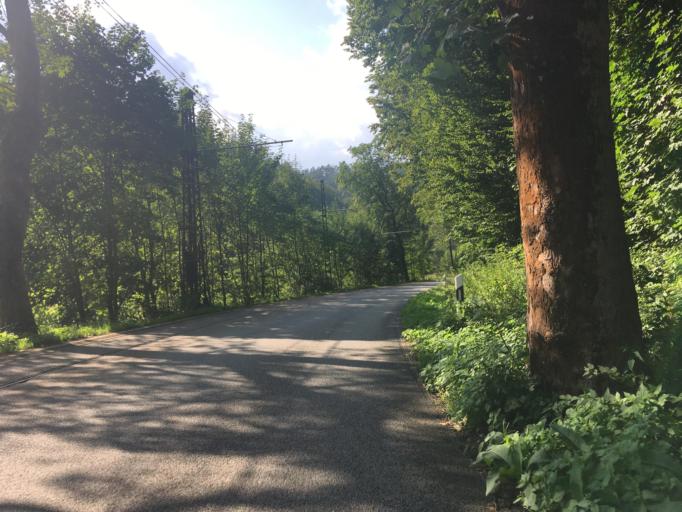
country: DE
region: Saxony
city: Bad Schandau
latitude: 50.9294
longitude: 14.2101
